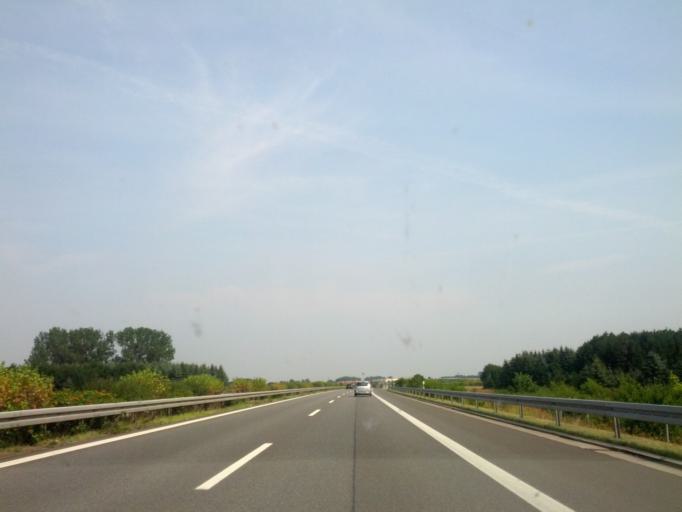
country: DE
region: Mecklenburg-Vorpommern
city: Grimmen
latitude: 54.0882
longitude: 13.0632
